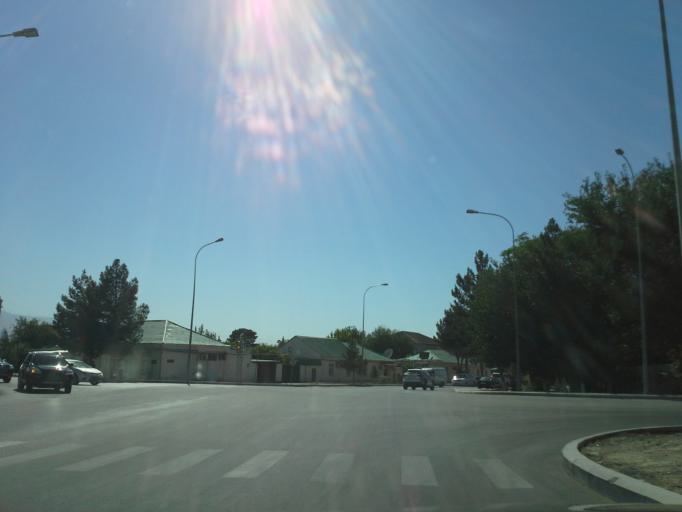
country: TM
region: Ahal
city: Ashgabat
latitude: 37.9520
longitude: 58.3890
